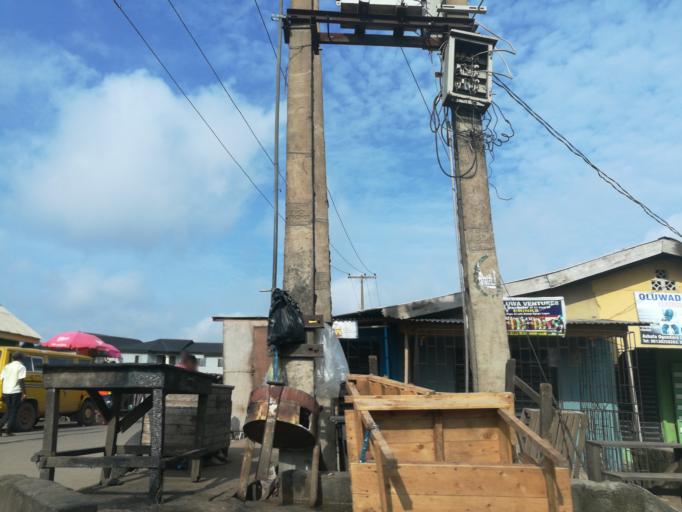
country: NG
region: Lagos
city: Agege
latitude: 6.6221
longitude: 3.3128
